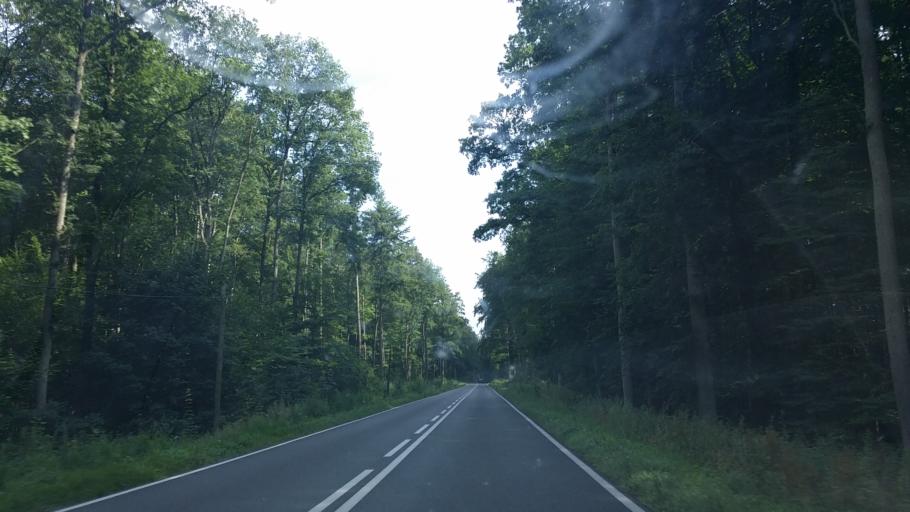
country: PL
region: West Pomeranian Voivodeship
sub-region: Powiat mysliborski
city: Barlinek
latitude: 52.9458
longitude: 15.1876
